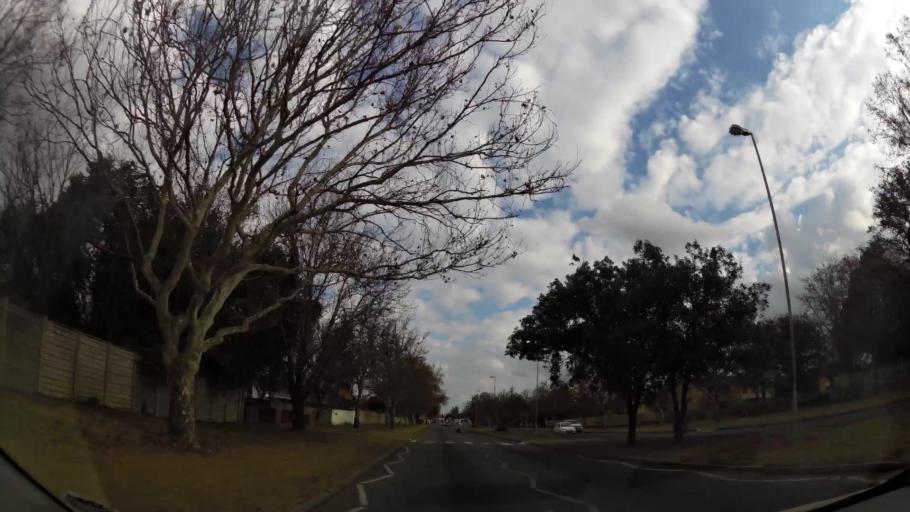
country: ZA
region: Orange Free State
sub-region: Fezile Dabi District Municipality
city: Sasolburg
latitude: -26.8075
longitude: 27.8291
